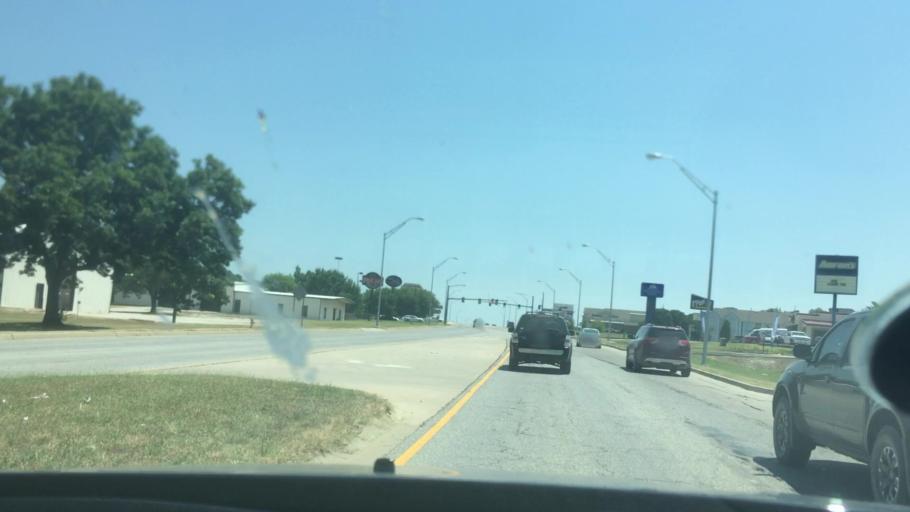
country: US
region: Oklahoma
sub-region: Pontotoc County
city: Ada
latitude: 34.7897
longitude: -96.6680
